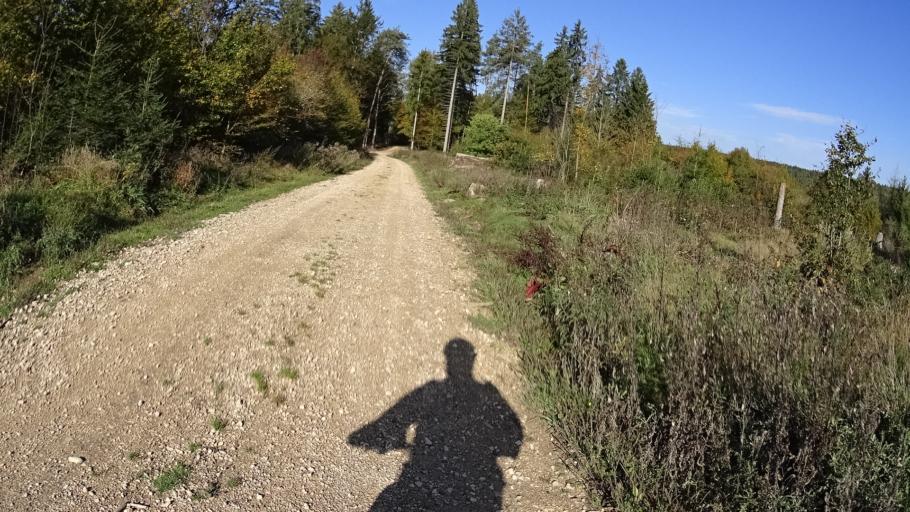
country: DE
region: Bavaria
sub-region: Upper Bavaria
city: Bohmfeld
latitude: 48.8855
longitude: 11.3572
